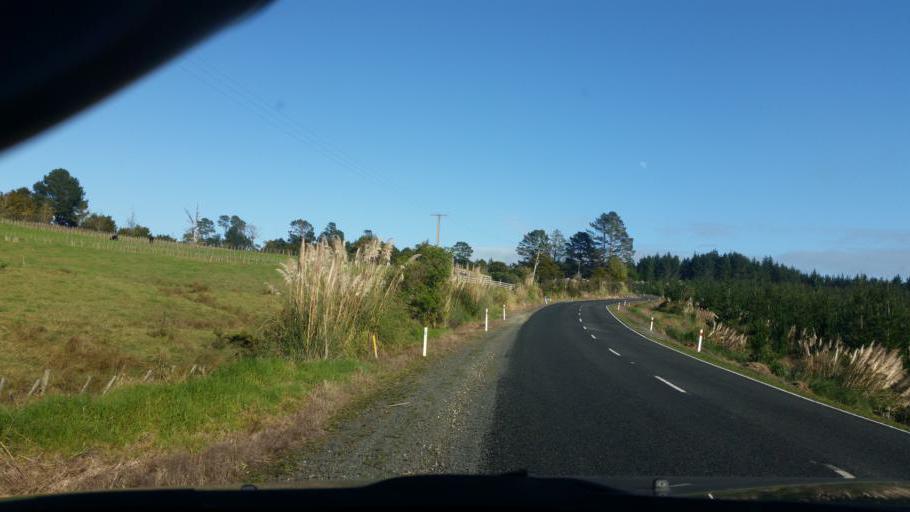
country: NZ
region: Auckland
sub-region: Auckland
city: Wellsford
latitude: -36.2230
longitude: 174.4571
